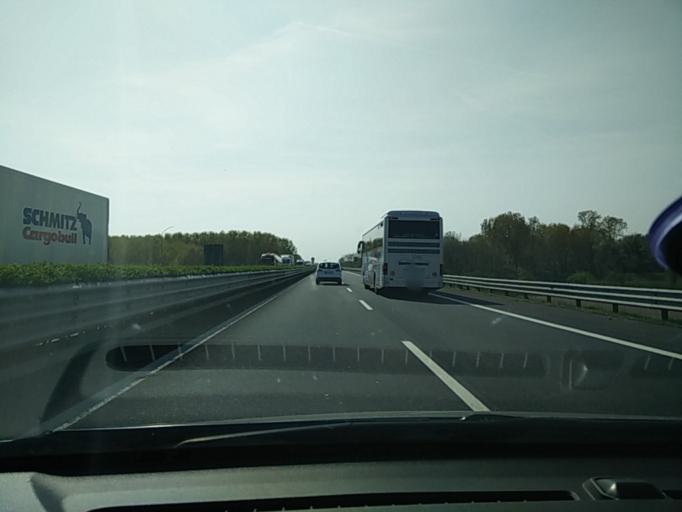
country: IT
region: Friuli Venezia Giulia
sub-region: Provincia di Udine
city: Ronchis
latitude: 45.8150
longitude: 12.9971
